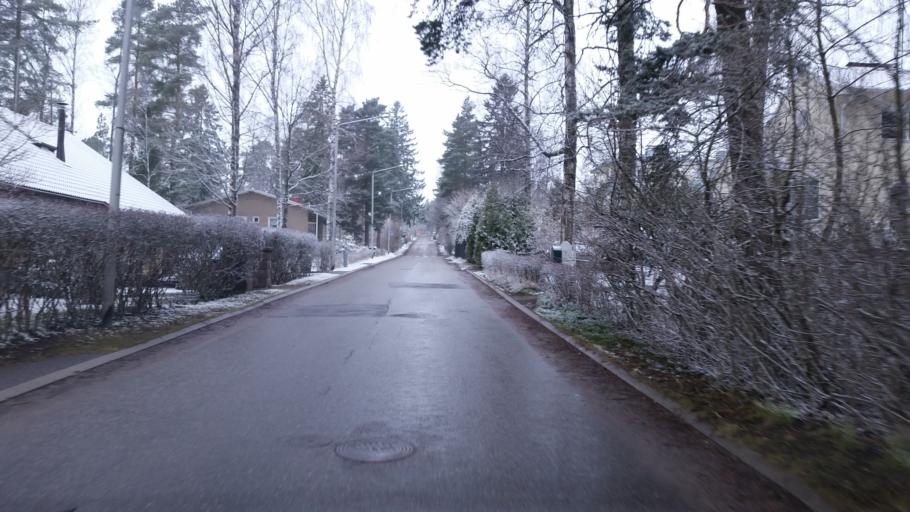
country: FI
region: Uusimaa
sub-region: Helsinki
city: Otaniemi
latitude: 60.1640
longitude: 24.8000
